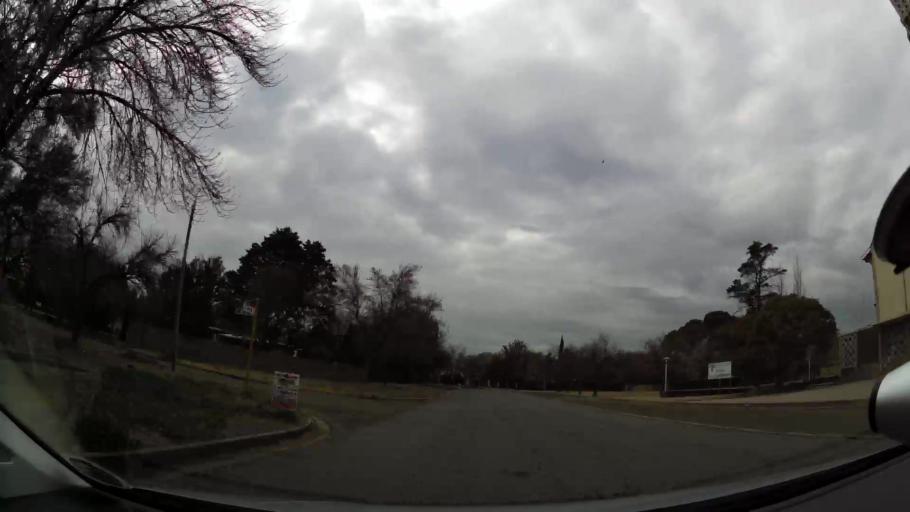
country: ZA
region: Orange Free State
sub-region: Fezile Dabi District Municipality
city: Kroonstad
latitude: -27.6721
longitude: 27.2496
